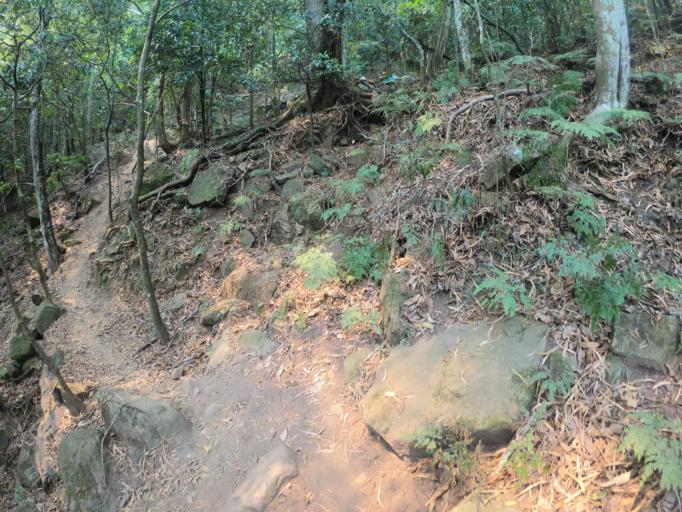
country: AU
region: New South Wales
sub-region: Wollongong
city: Mount Keira
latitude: -34.4043
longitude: 150.8520
